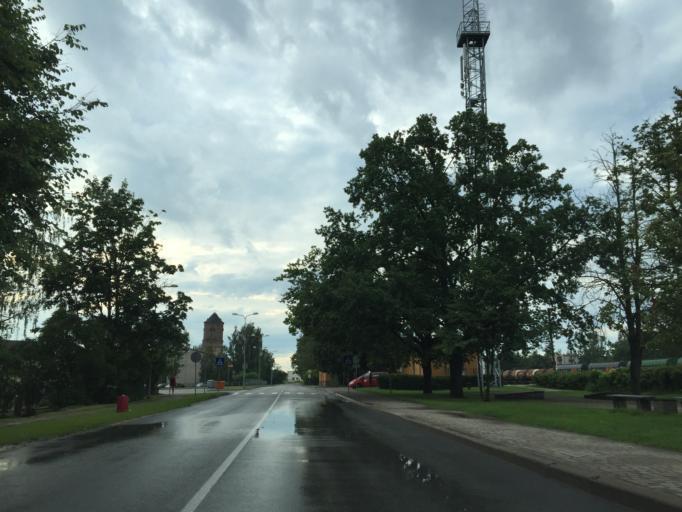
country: LV
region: Dobeles Rajons
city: Dobele
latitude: 56.6278
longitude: 23.2858
